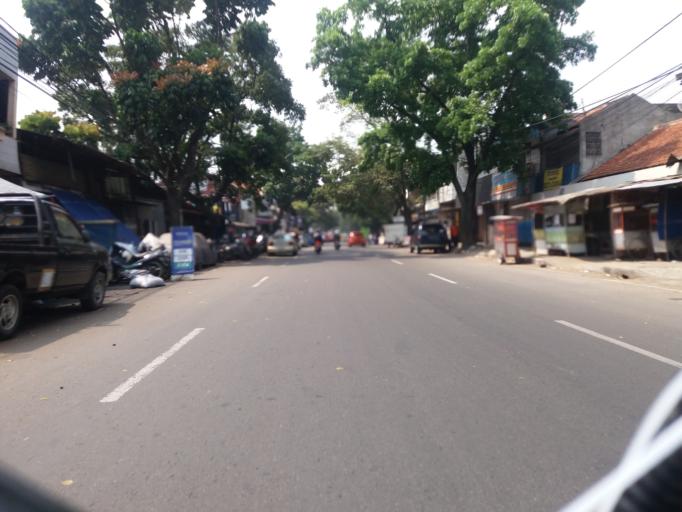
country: ID
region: West Java
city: Bandung
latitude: -6.9148
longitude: 107.5826
